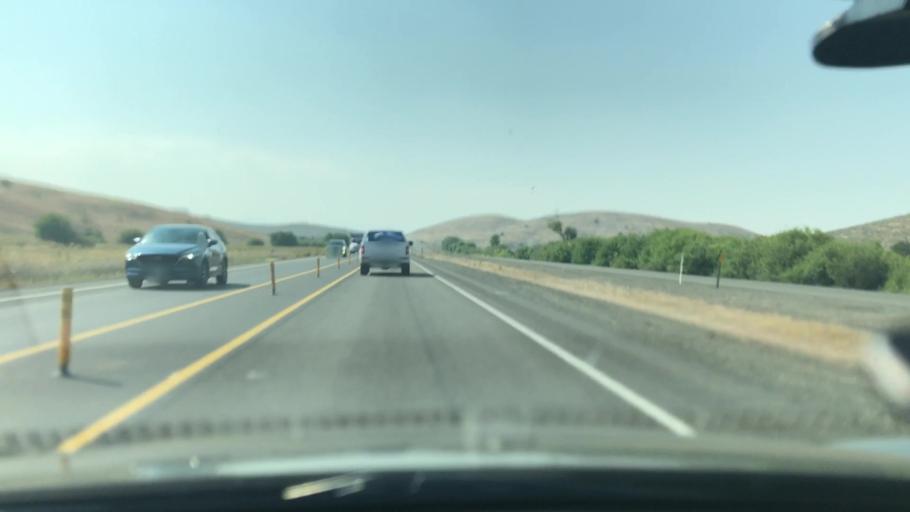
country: US
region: Oregon
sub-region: Baker County
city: Baker City
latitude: 44.6778
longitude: -117.6460
